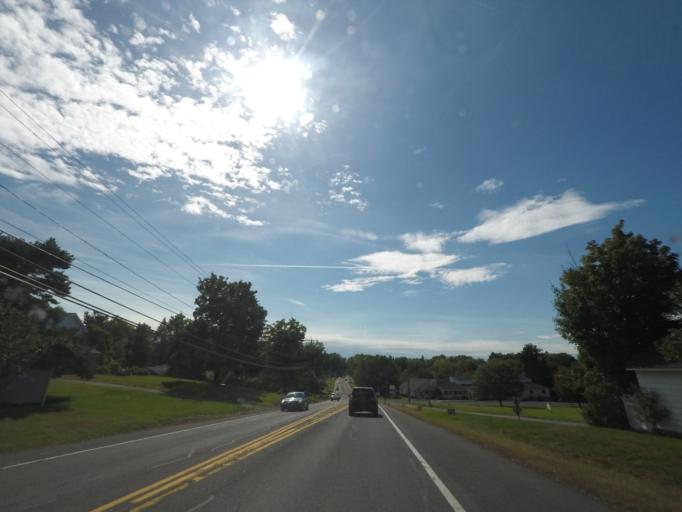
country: US
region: New York
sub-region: Rensselaer County
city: East Greenbush
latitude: 42.6170
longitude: -73.7026
